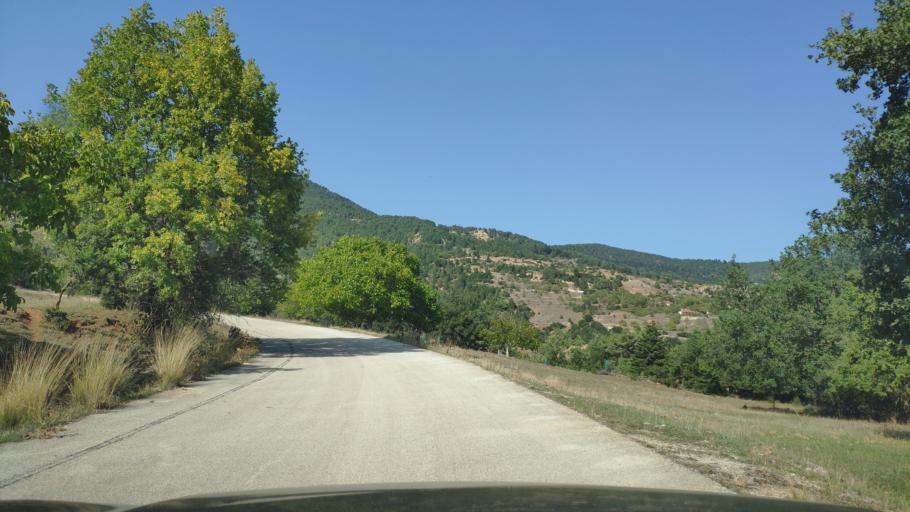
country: GR
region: West Greece
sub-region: Nomos Achaias
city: Aiyira
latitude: 37.9921
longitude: 22.3572
